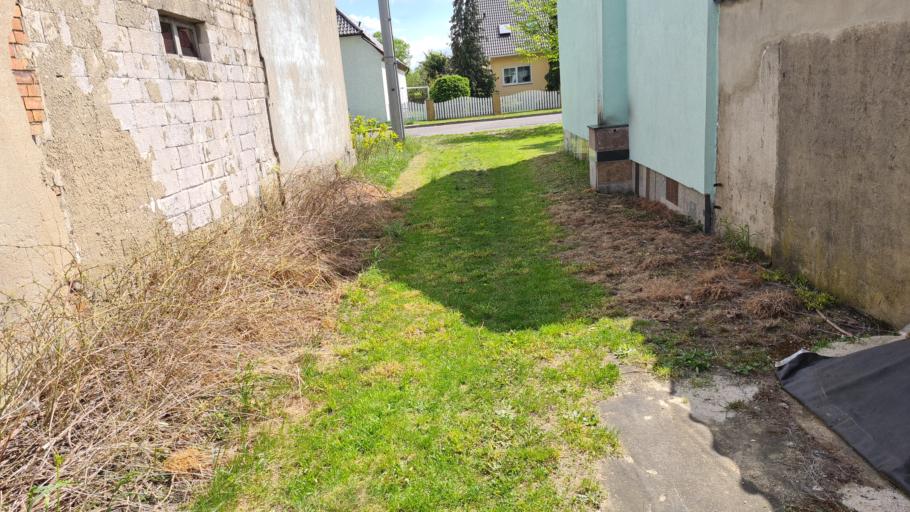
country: DE
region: Brandenburg
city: Grossraschen
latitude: 51.5880
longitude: 14.0352
